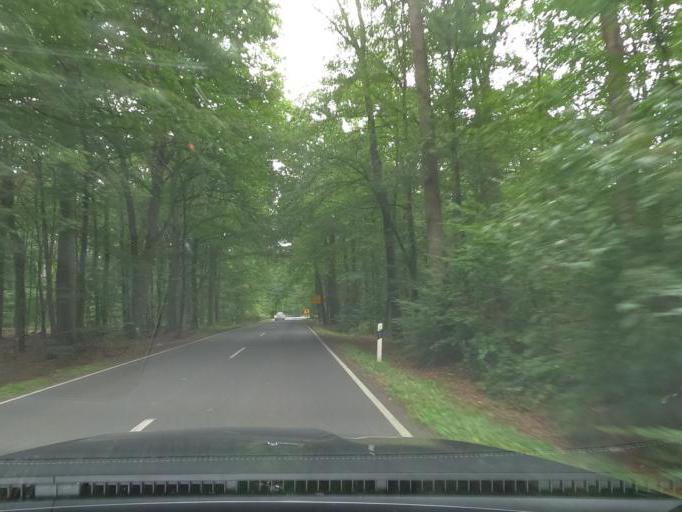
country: DE
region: Lower Saxony
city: Sehnde
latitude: 52.3115
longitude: 9.8933
